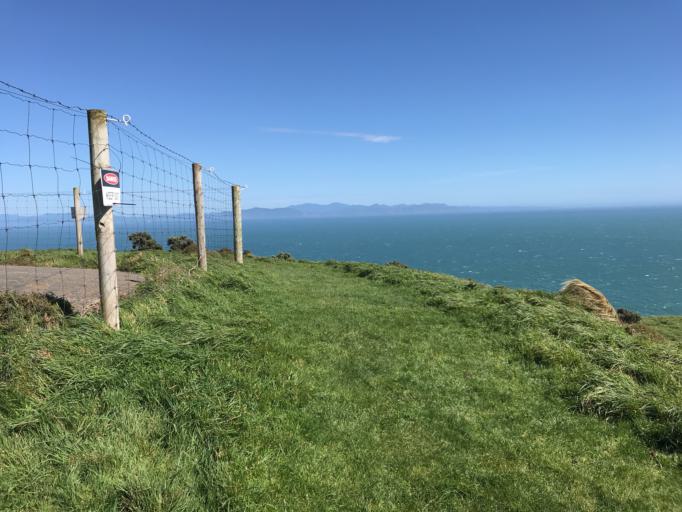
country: NZ
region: Wellington
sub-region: Wellington City
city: Kelburn
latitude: -41.2222
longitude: 174.6961
